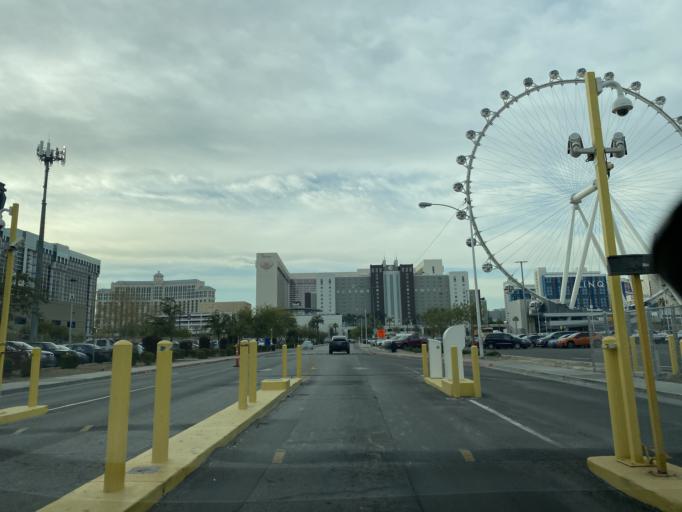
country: US
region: Nevada
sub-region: Clark County
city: Paradise
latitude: 36.1163
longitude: -115.1648
